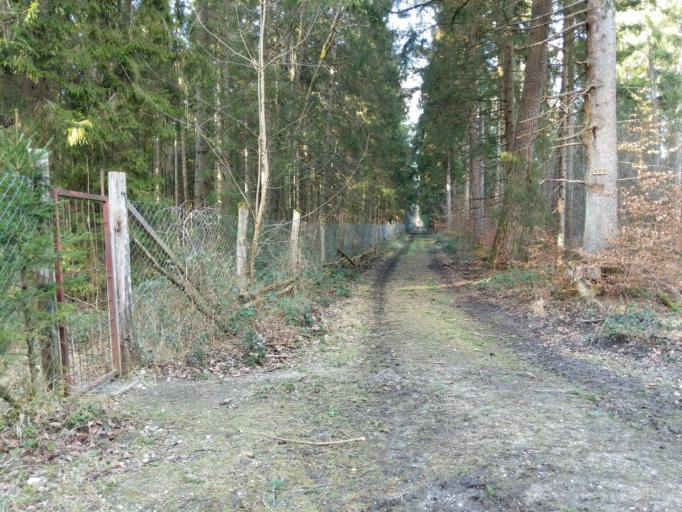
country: DE
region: Bavaria
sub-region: Upper Bavaria
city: Zorneding
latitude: 48.1012
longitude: 11.8463
